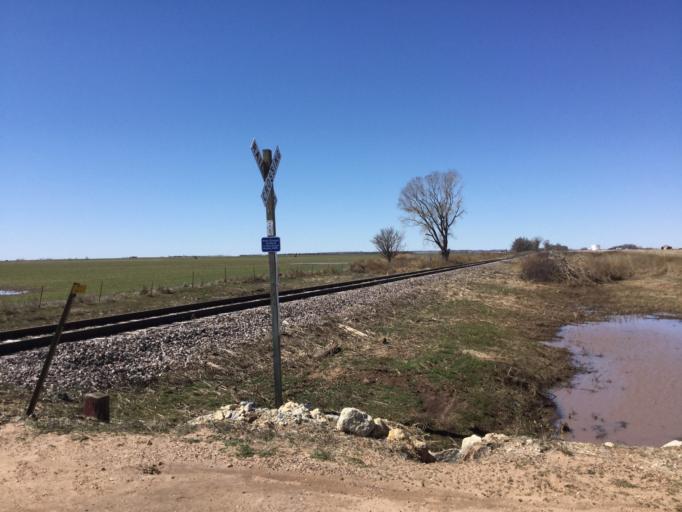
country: US
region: Kansas
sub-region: Barber County
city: Medicine Lodge
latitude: 37.2508
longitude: -98.4959
